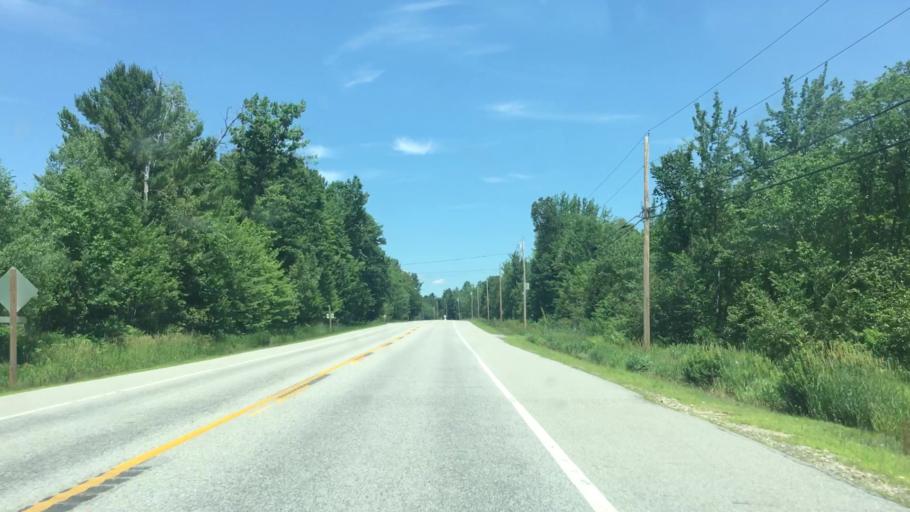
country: US
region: Maine
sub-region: Androscoggin County
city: Livermore
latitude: 44.3924
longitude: -70.2301
